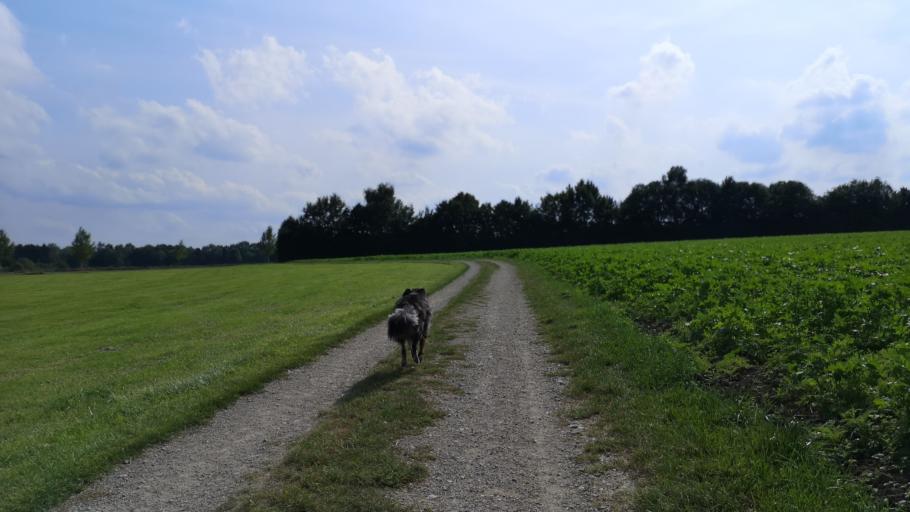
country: DE
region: Bavaria
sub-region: Upper Bavaria
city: Poing
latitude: 48.1801
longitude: 11.8220
